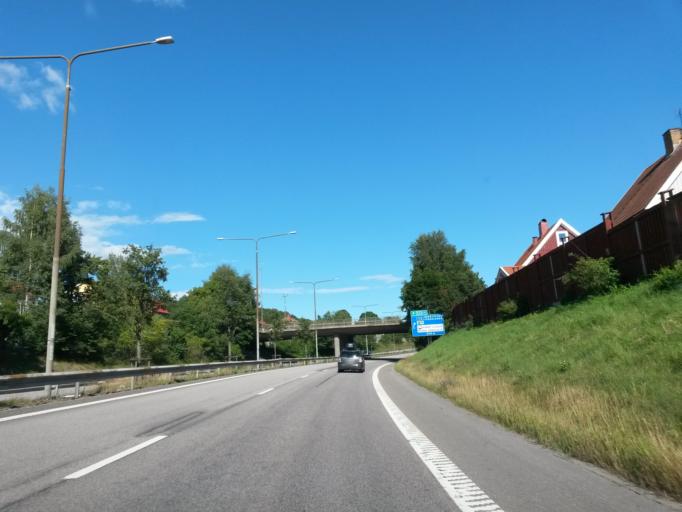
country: SE
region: Vaestra Goetaland
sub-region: Uddevalla Kommun
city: Uddevalla
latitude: 58.3563
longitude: 11.9414
